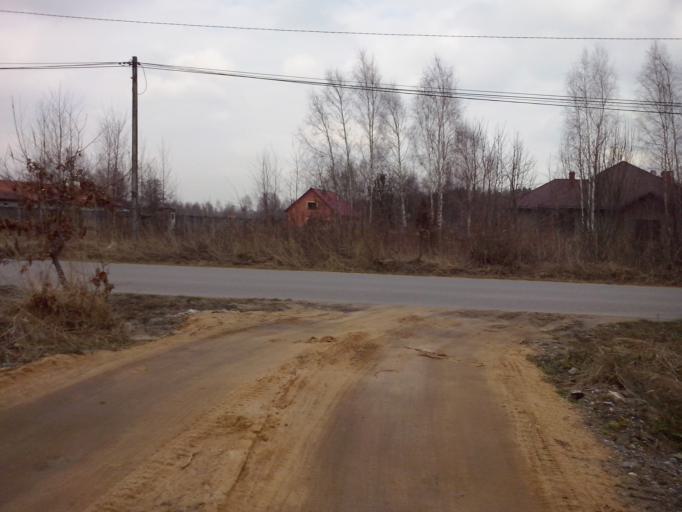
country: PL
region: Subcarpathian Voivodeship
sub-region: Powiat nizanski
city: Krzeszow
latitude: 50.4144
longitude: 22.3395
